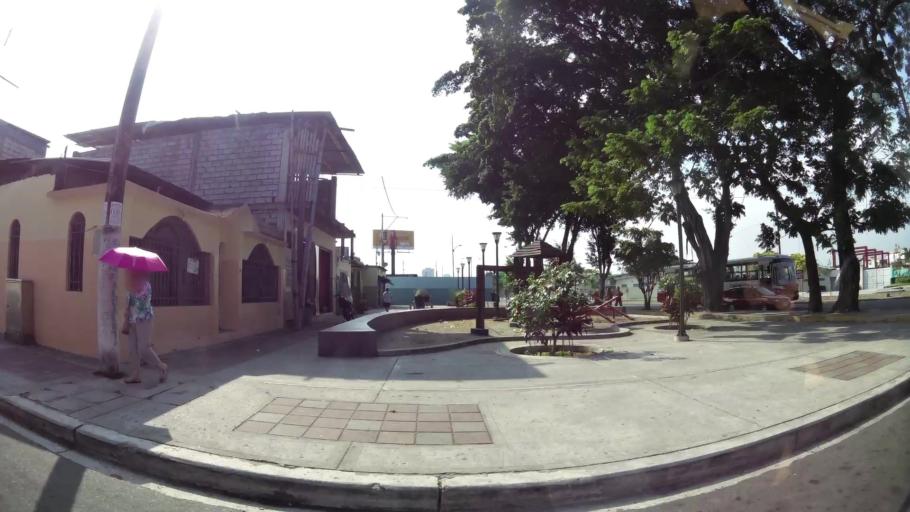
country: EC
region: Guayas
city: Guayaquil
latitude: -2.1879
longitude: -79.9083
